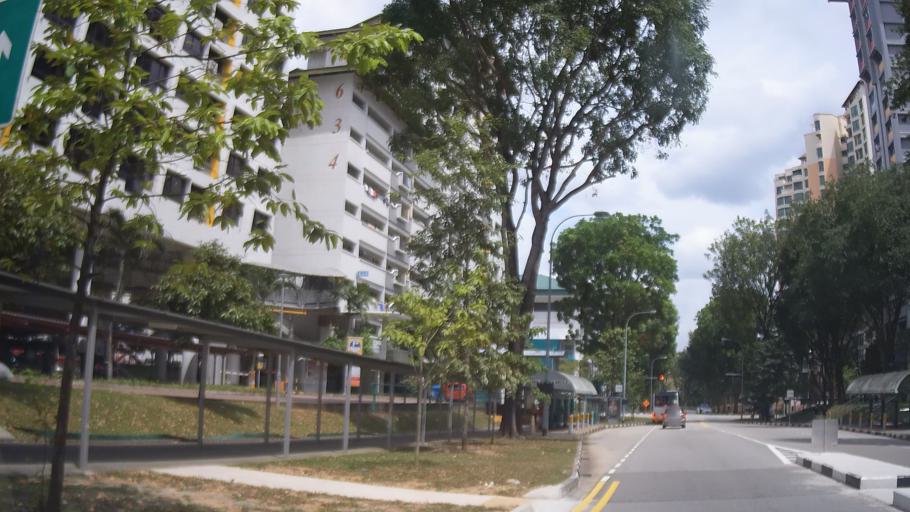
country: MY
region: Johor
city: Johor Bahru
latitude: 1.3962
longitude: 103.7490
